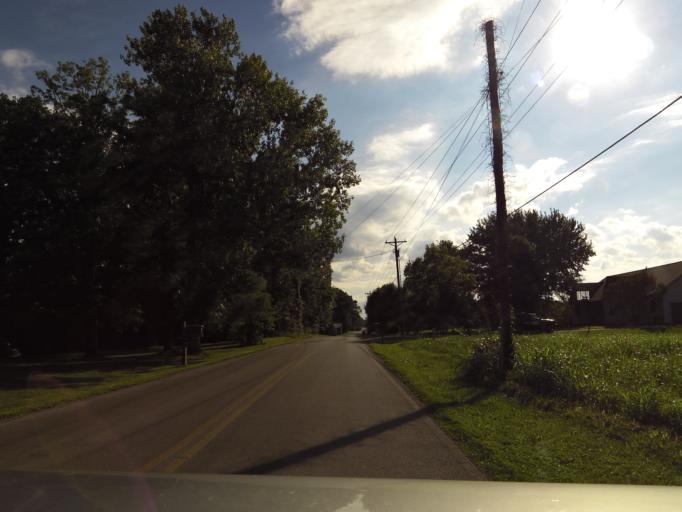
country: US
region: Tennessee
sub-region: Loudon County
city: Greenback
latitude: 35.6680
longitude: -84.0701
